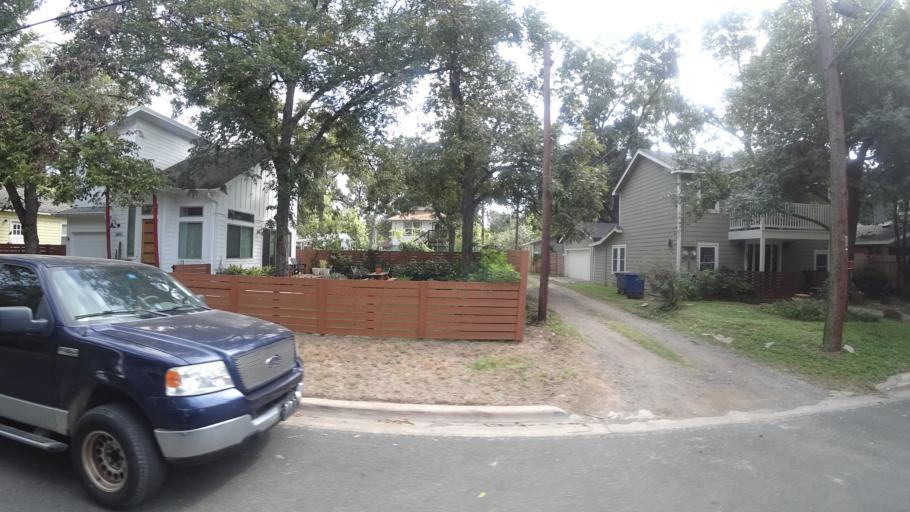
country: US
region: Texas
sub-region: Travis County
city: Austin
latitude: 30.2526
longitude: -97.7160
